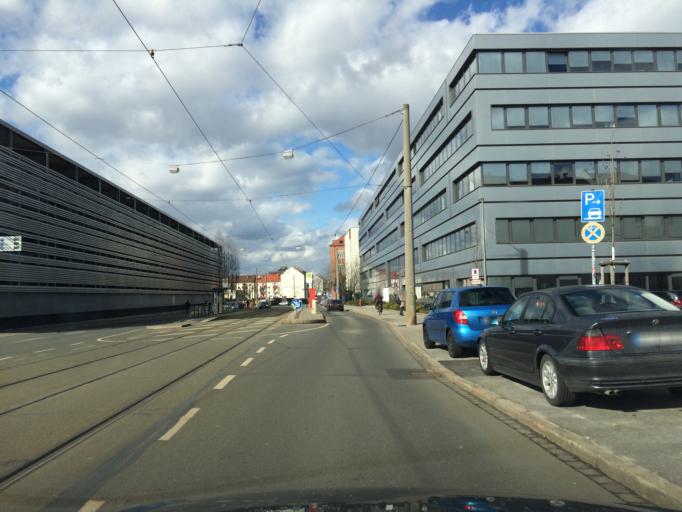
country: DE
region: Bavaria
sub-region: Regierungsbezirk Mittelfranken
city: Nuernberg
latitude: 49.4363
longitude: 11.0753
